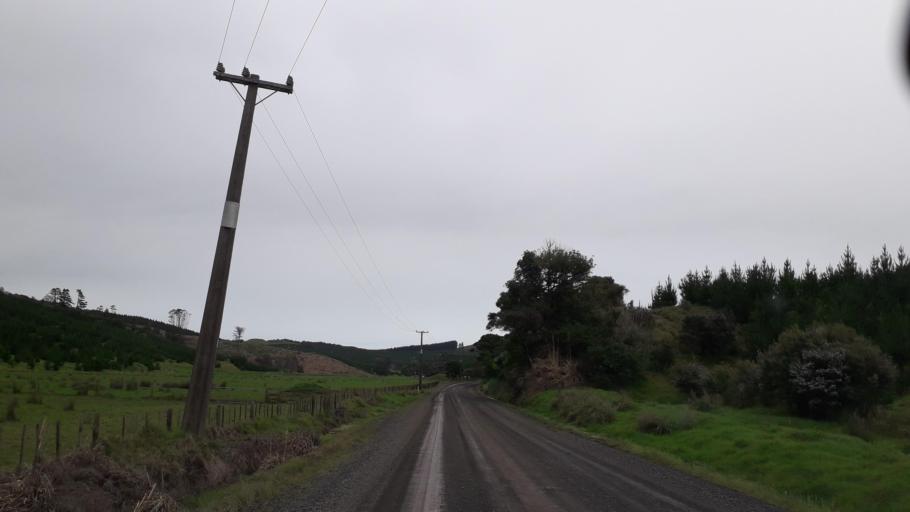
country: NZ
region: Northland
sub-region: Far North District
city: Ahipara
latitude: -35.4265
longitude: 173.3563
